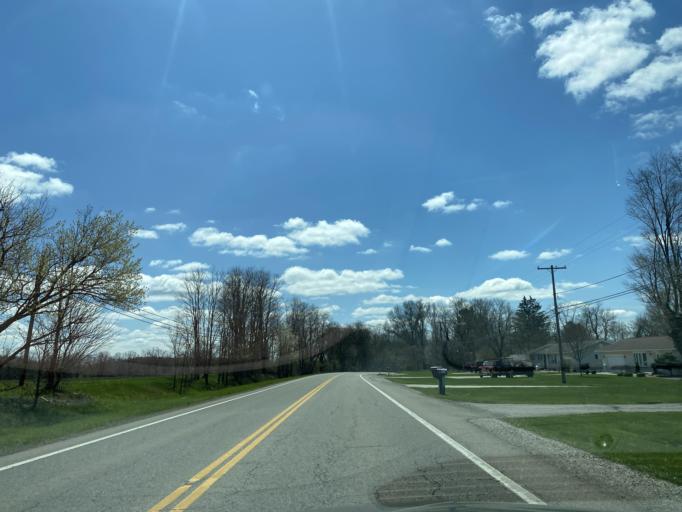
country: US
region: Ohio
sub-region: Wayne County
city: Wooster
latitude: 40.7664
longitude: -81.9728
